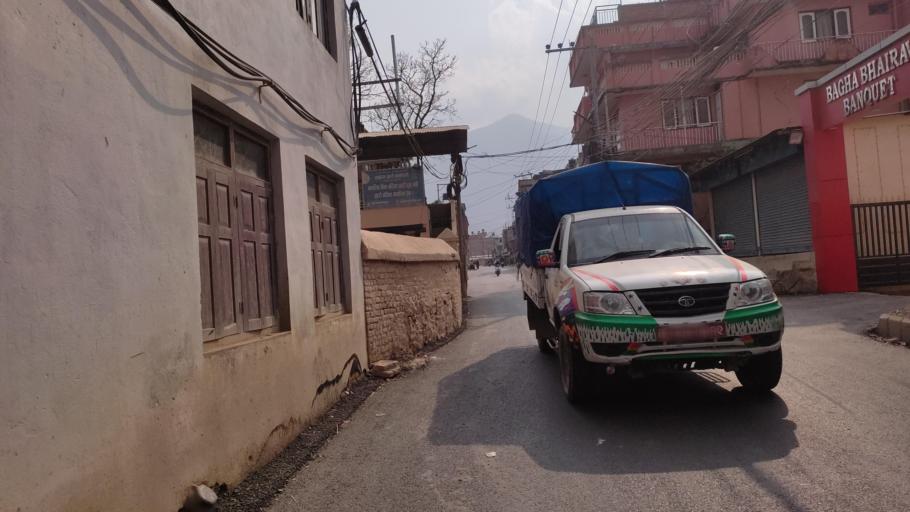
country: NP
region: Central Region
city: Kirtipur
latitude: 27.6732
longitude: 85.2746
